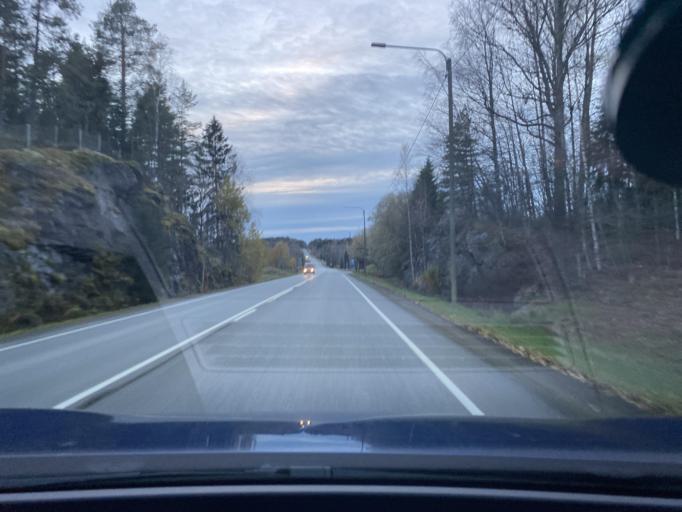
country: FI
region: Uusimaa
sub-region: Helsinki
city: Saukkola
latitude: 60.3858
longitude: 24.0001
